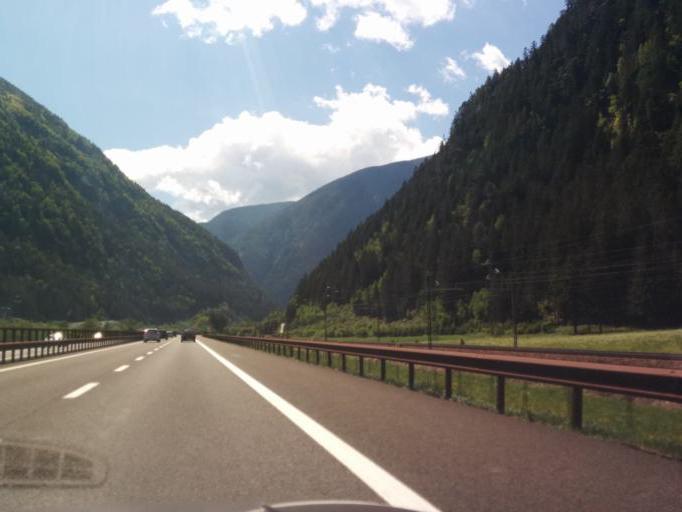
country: IT
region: Trentino-Alto Adige
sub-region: Bolzano
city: Campo di Trens
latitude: 46.8338
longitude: 11.5318
